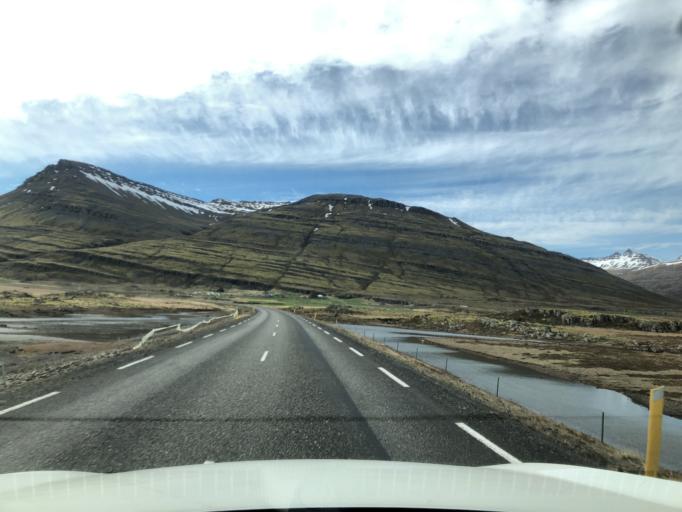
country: IS
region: East
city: Eskifjoerdur
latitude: 64.7716
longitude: -14.0525
